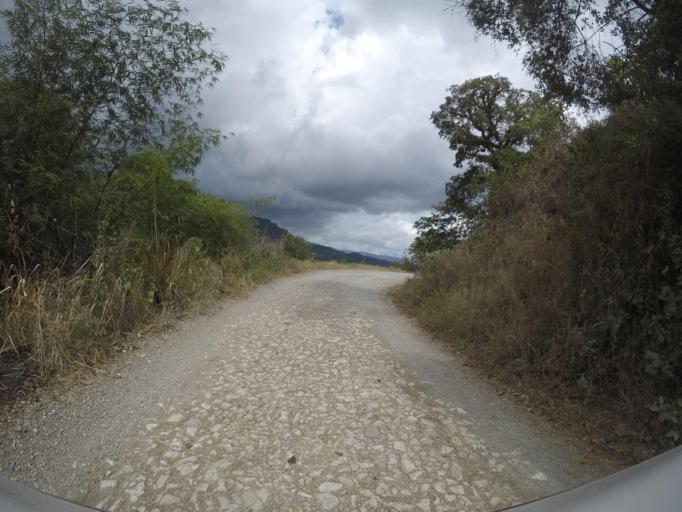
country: TL
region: Baucau
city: Baucau
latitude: -8.6181
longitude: 126.6613
